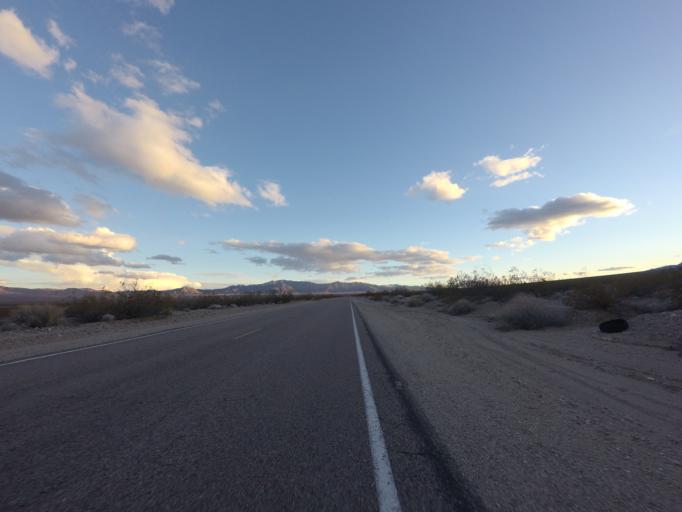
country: US
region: Nevada
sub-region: Clark County
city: Sandy Valley
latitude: 35.4336
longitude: -115.3861
